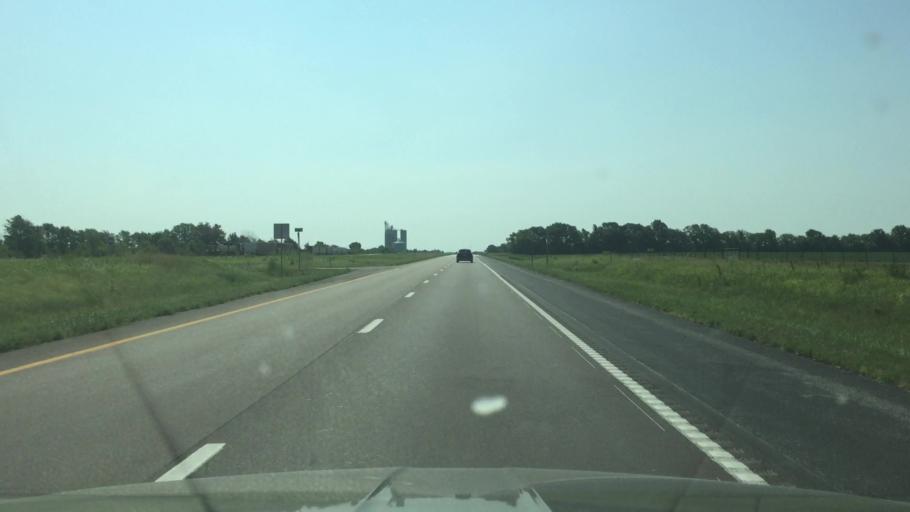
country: US
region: Missouri
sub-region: Pettis County
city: La Monte
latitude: 38.7566
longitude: -93.3645
